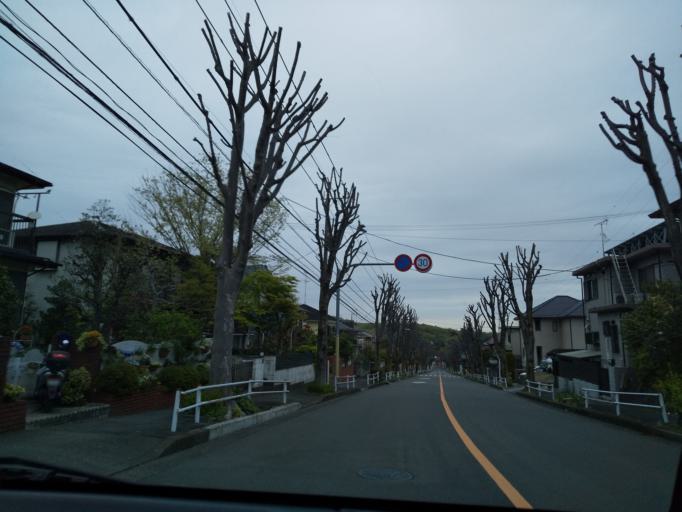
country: JP
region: Tokyo
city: Hino
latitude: 35.6346
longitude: 139.3784
